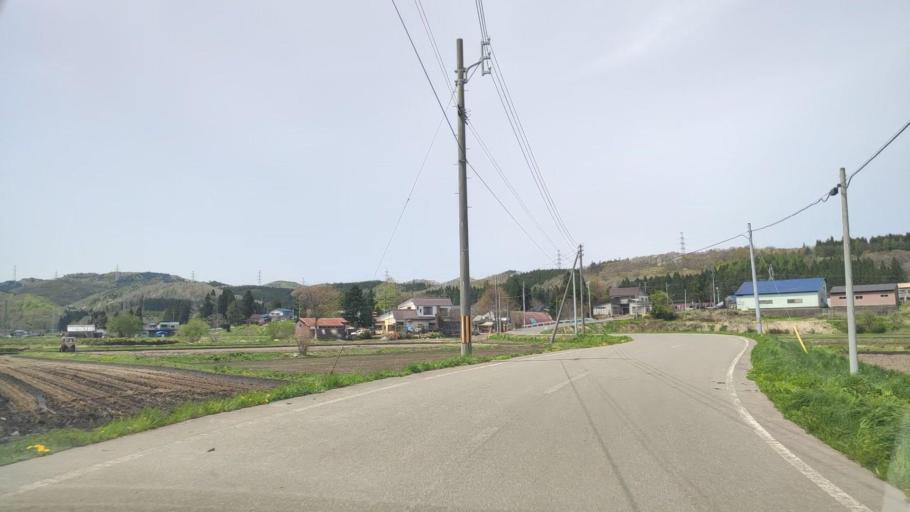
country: JP
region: Aomori
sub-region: Misawa Shi
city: Inuotose
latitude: 40.7871
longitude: 141.1103
